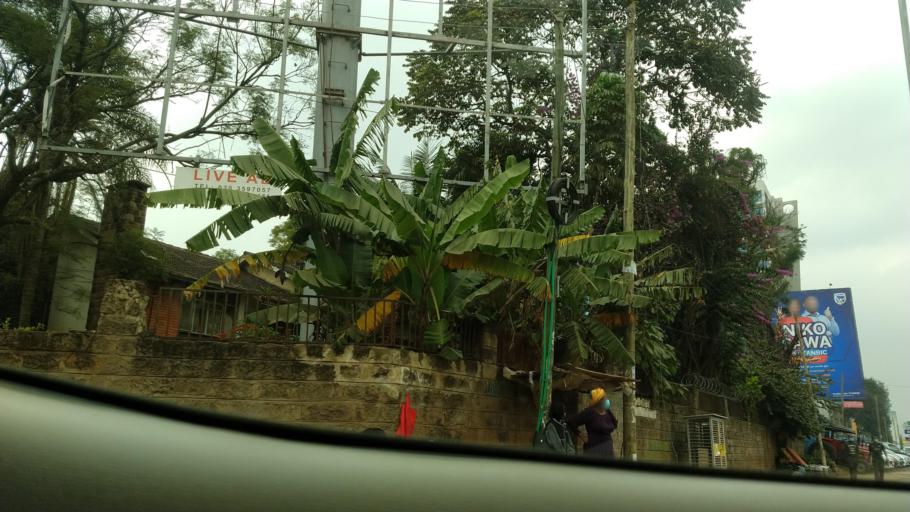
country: KE
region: Nairobi Area
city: Nairobi
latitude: -1.2998
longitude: 36.7796
